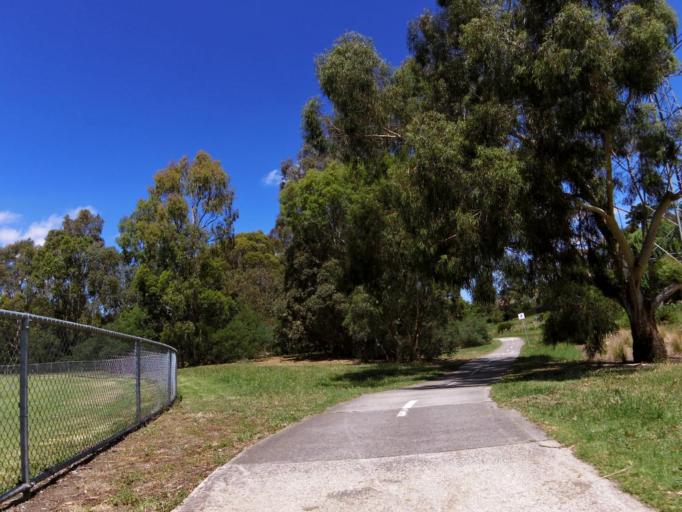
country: AU
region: Victoria
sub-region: Moreland
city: Coburg
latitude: -37.7496
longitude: 144.9813
